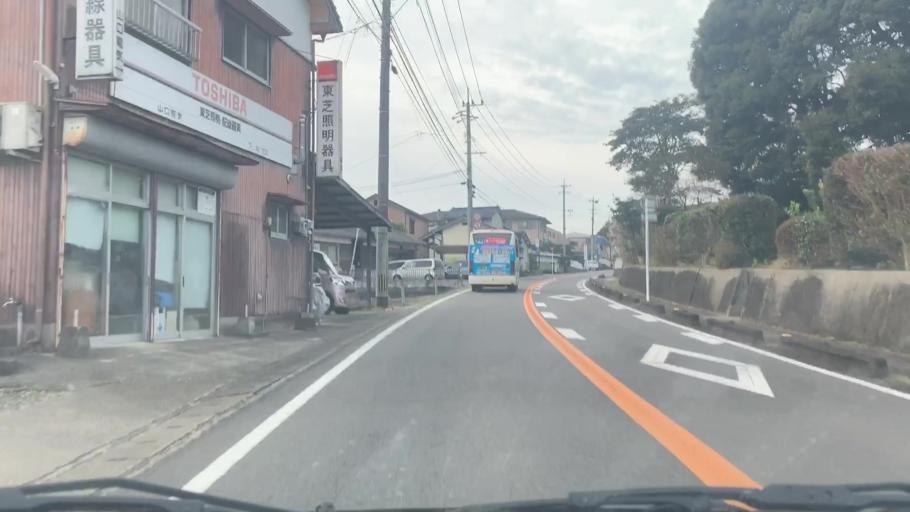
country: JP
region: Saga Prefecture
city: Ureshinomachi-shimojuku
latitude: 33.1214
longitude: 130.0021
